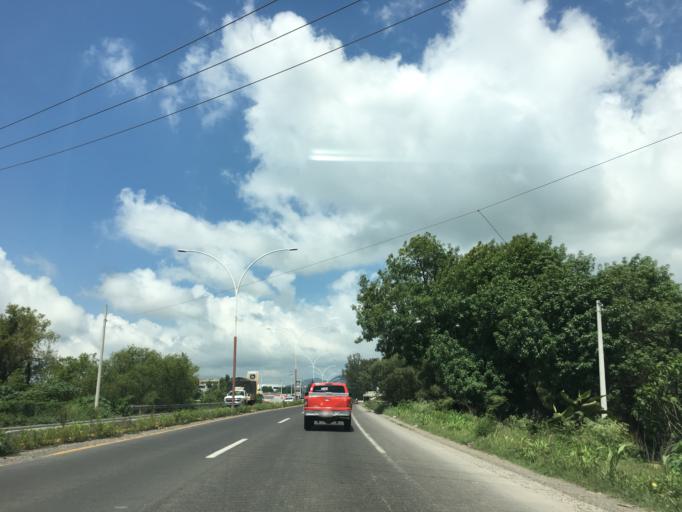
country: MX
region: Nayarit
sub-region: Tepic
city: La Corregidora
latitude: 21.4675
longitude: -104.8522
